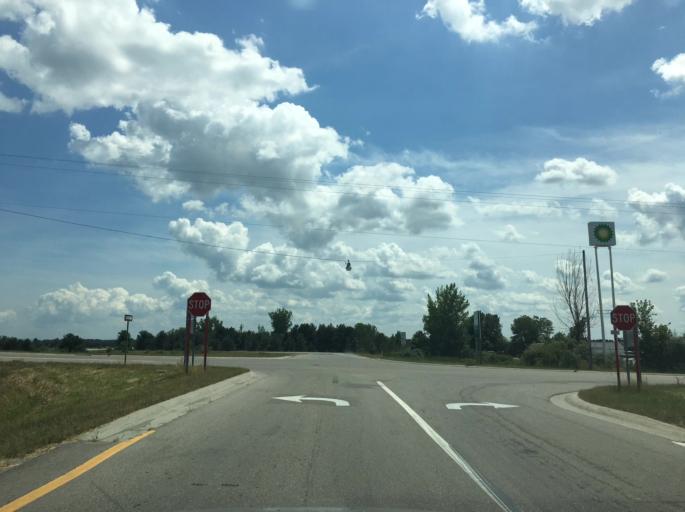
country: US
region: Michigan
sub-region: Bay County
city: Pinconning
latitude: 43.8544
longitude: -84.0232
